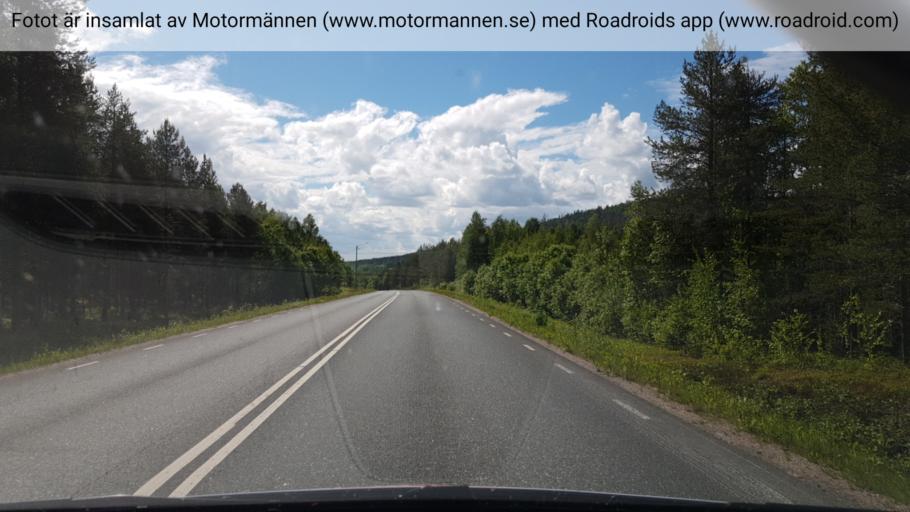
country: SE
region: Norrbotten
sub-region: Overtornea Kommun
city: OEvertornea
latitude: 66.3702
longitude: 23.6501
